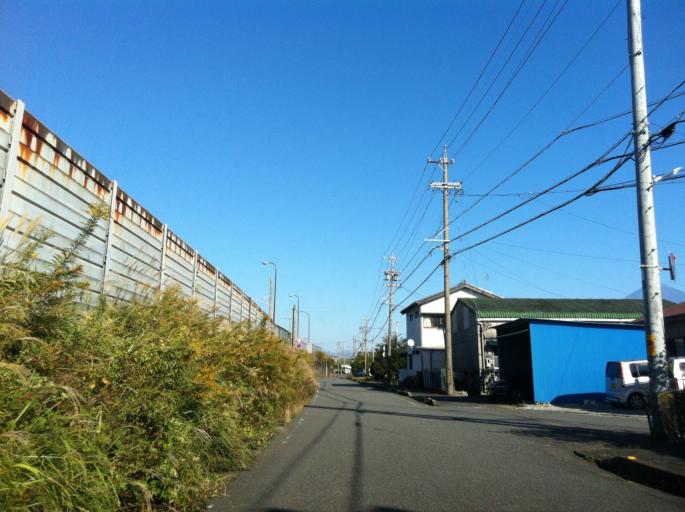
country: JP
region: Shizuoka
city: Fuji
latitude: 35.1193
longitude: 138.6236
